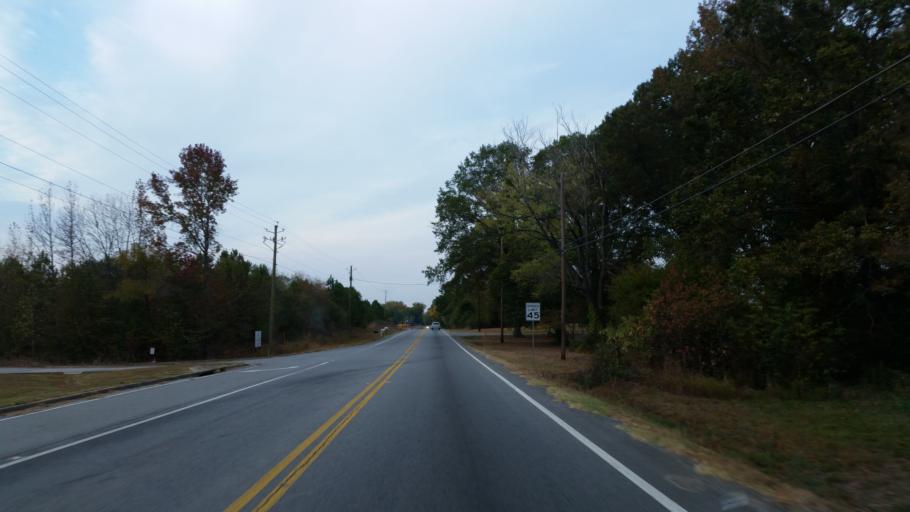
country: US
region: Georgia
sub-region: Gordon County
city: Calhoun
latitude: 34.5609
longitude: -84.9372
